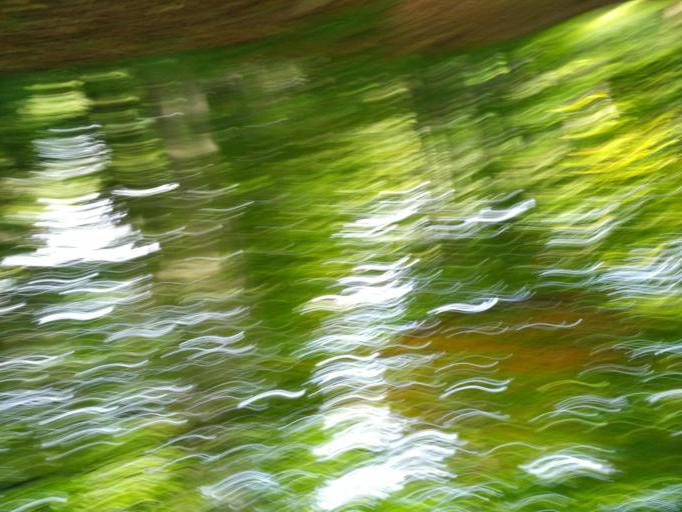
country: PL
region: Subcarpathian Voivodeship
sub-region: Powiat strzyzowski
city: Frysztak
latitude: 49.8900
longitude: 21.5570
